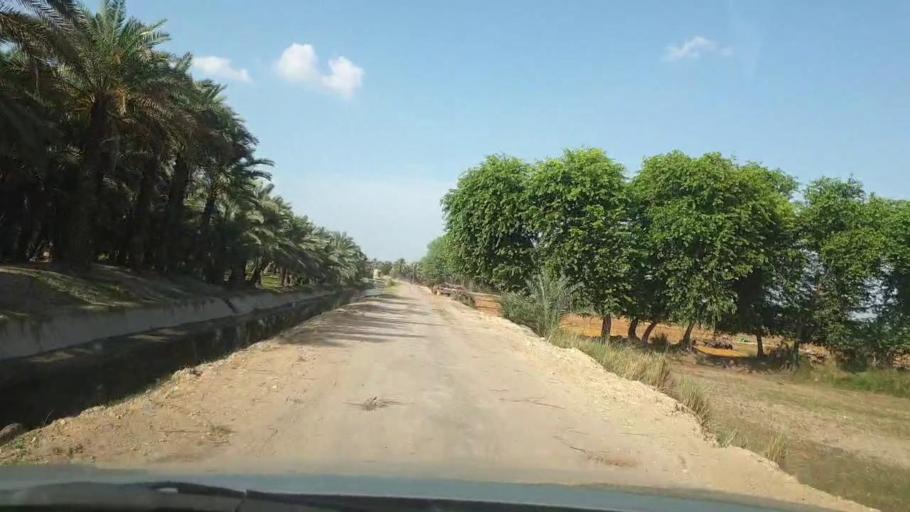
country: PK
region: Sindh
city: Sukkur
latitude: 27.6498
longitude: 68.8265
